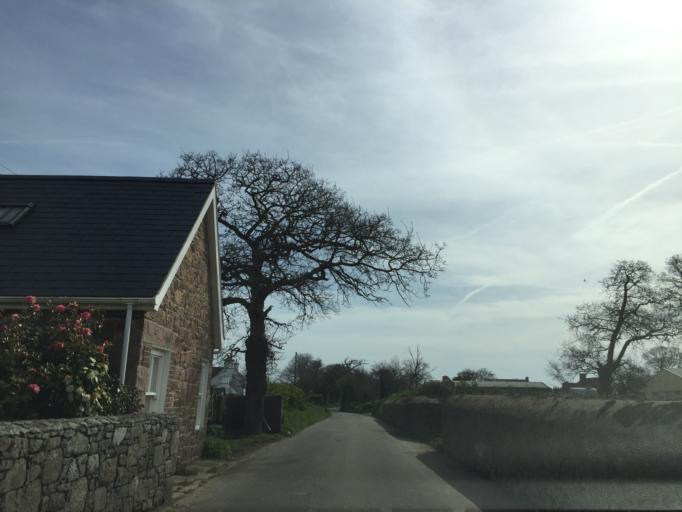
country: JE
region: St Helier
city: Saint Helier
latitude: 49.2289
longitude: -2.0402
